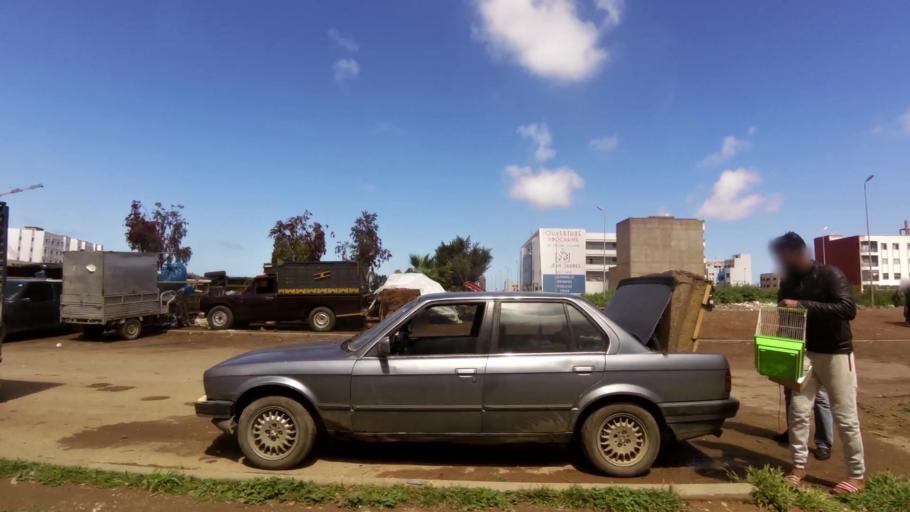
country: MA
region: Grand Casablanca
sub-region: Nouaceur
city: Dar Bouazza
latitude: 33.5371
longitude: -7.7306
